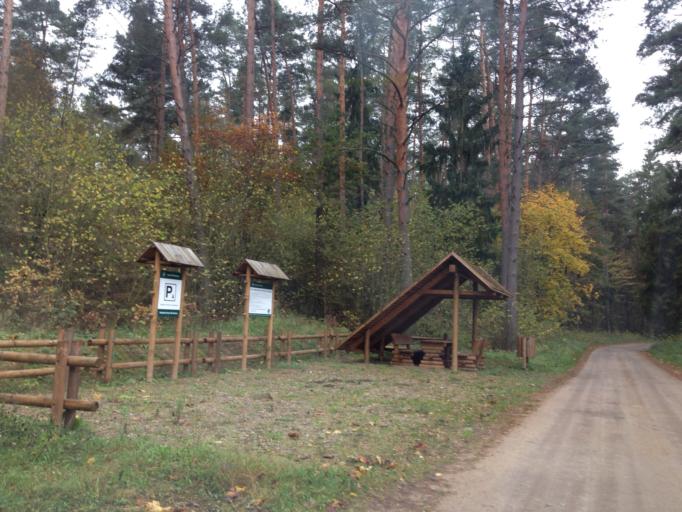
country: PL
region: Kujawsko-Pomorskie
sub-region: Powiat brodnicki
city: Bartniczka
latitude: 53.2722
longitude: 19.5726
